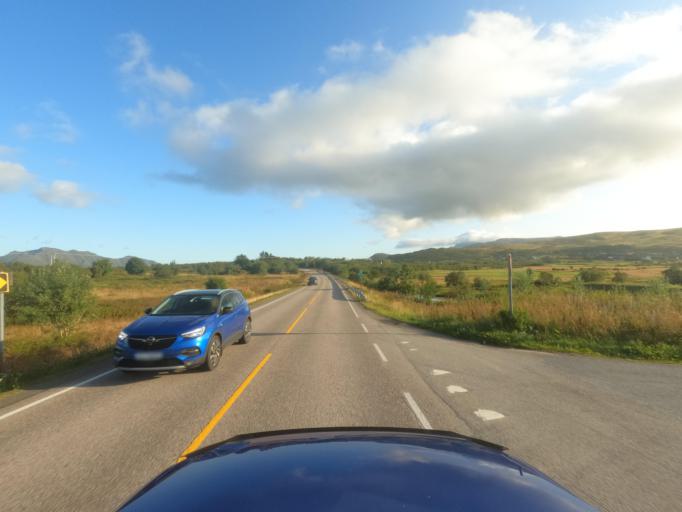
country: NO
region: Nordland
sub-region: Vestvagoy
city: Gravdal
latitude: 68.1455
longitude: 13.5464
